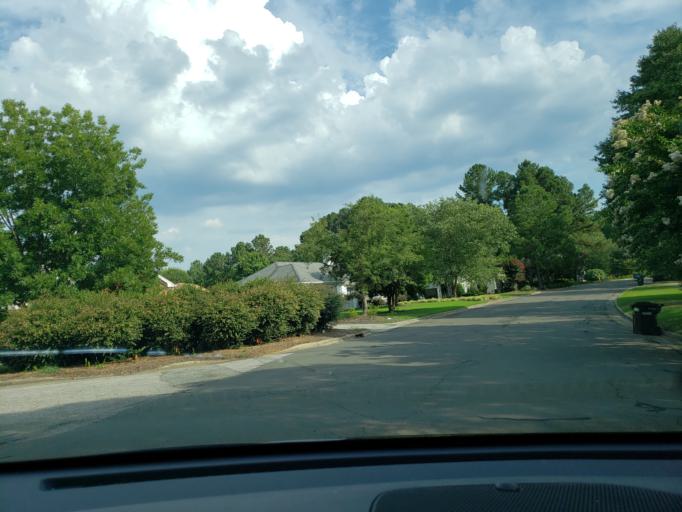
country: US
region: North Carolina
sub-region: Orange County
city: Chapel Hill
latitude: 35.9054
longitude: -78.9845
